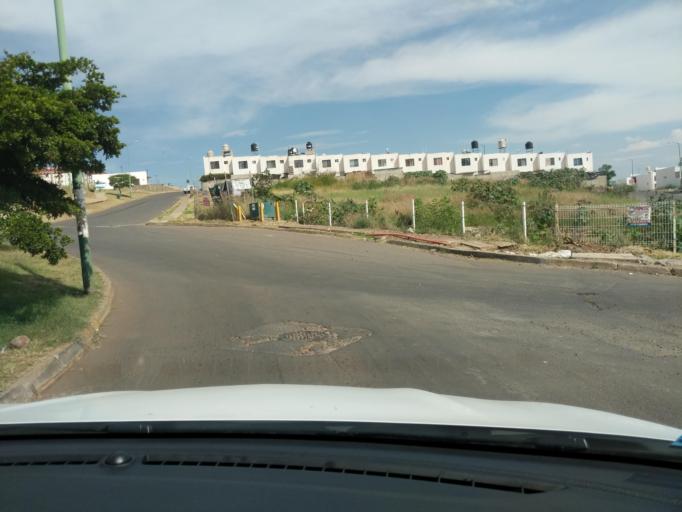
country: MX
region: Jalisco
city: San Jose del Castillo
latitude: 20.5208
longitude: -103.2297
